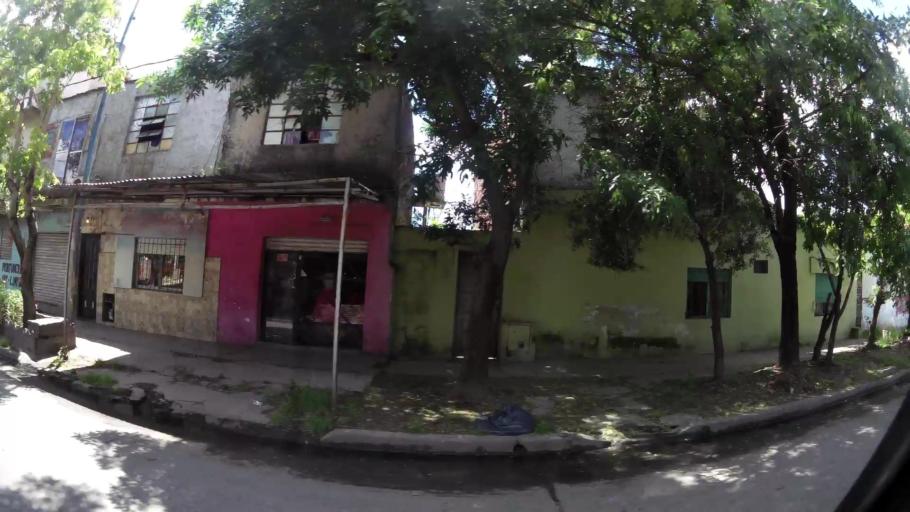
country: AR
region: Buenos Aires F.D.
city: Villa Lugano
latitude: -34.7007
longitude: -58.4378
